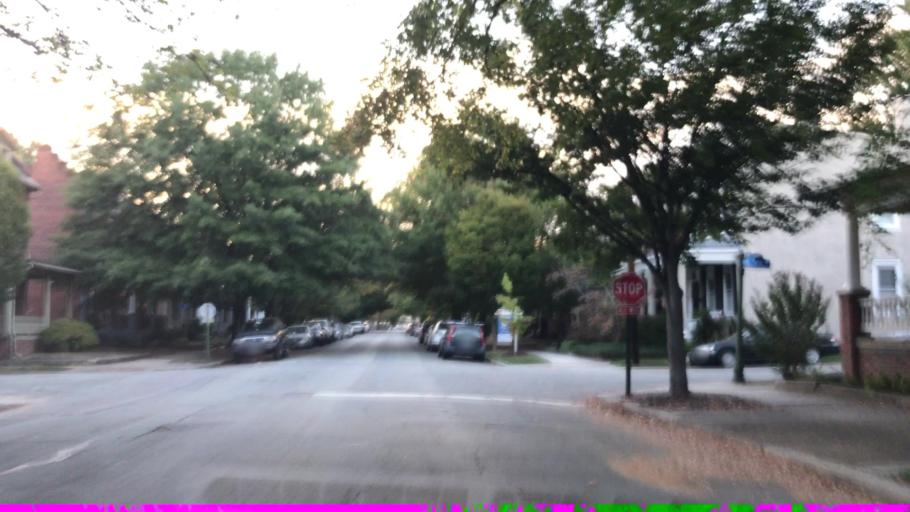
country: US
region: Virginia
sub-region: City of Richmond
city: Richmond
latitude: 37.5622
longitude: -77.4785
